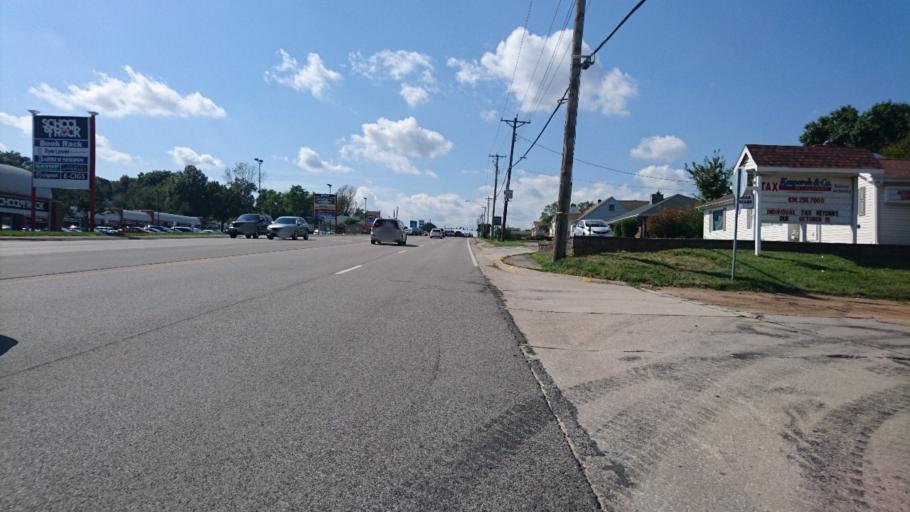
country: US
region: Missouri
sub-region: Saint Louis County
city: Winchester
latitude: 38.5931
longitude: -90.5251
